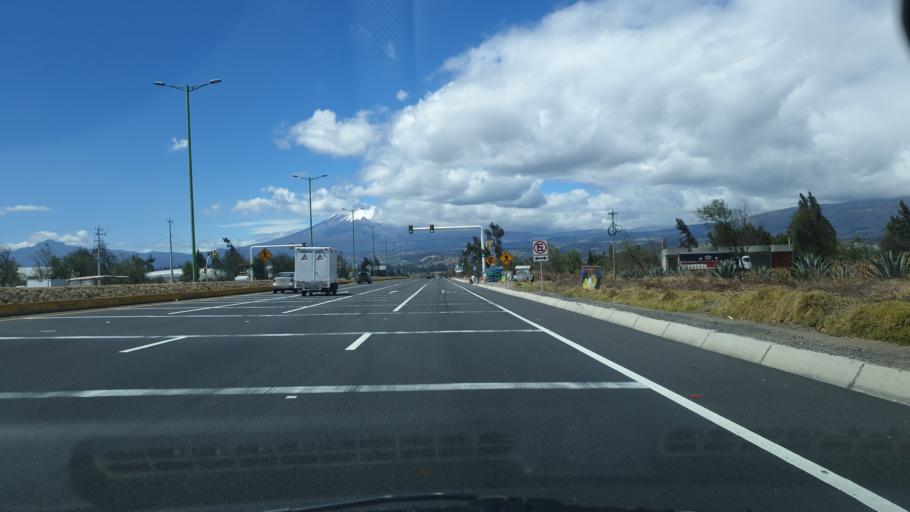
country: EC
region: Cotopaxi
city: Saquisili
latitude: -0.8789
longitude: -78.6483
